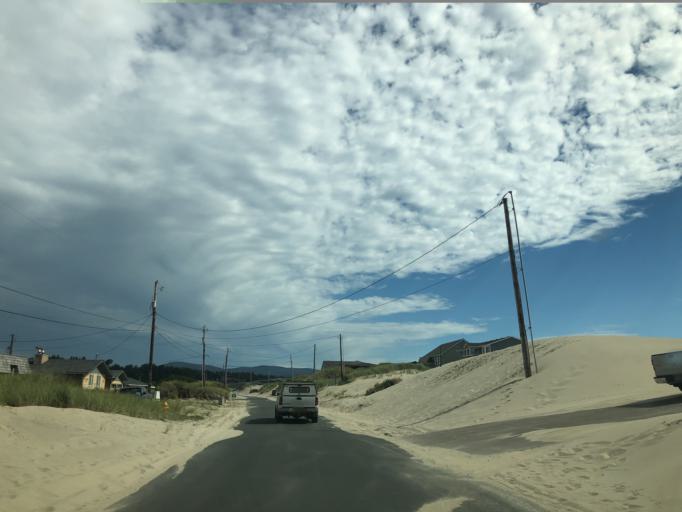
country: US
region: Oregon
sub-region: Lincoln County
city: Waldport
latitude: 44.4291
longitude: -124.0825
